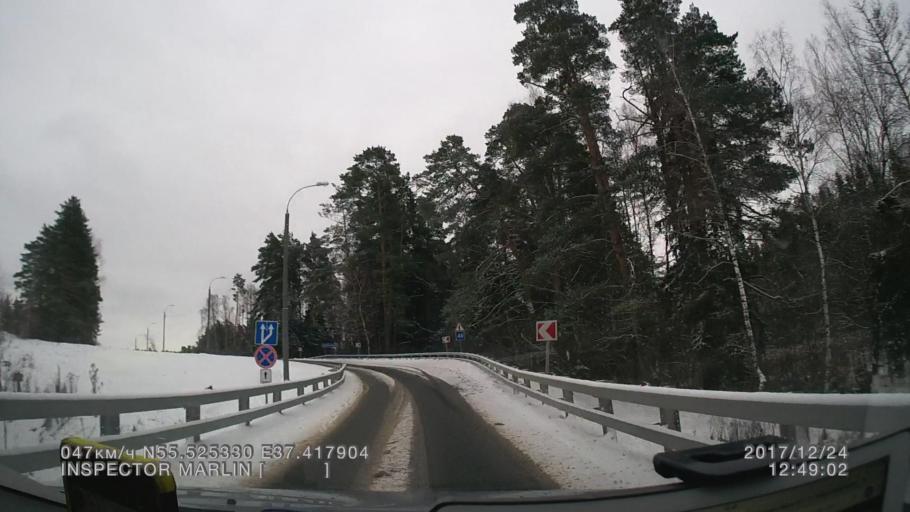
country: RU
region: Moskovskaya
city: Filimonki
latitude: 55.5253
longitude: 37.4179
